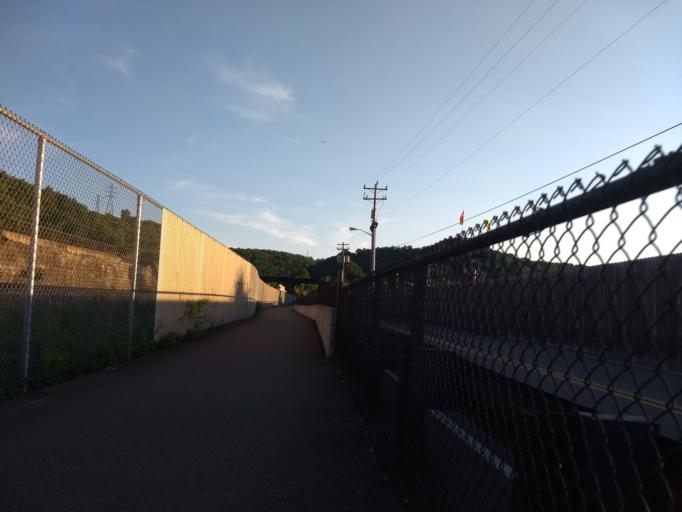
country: US
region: Pennsylvania
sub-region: Allegheny County
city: West Homestead
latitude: 40.3974
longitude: -79.9271
